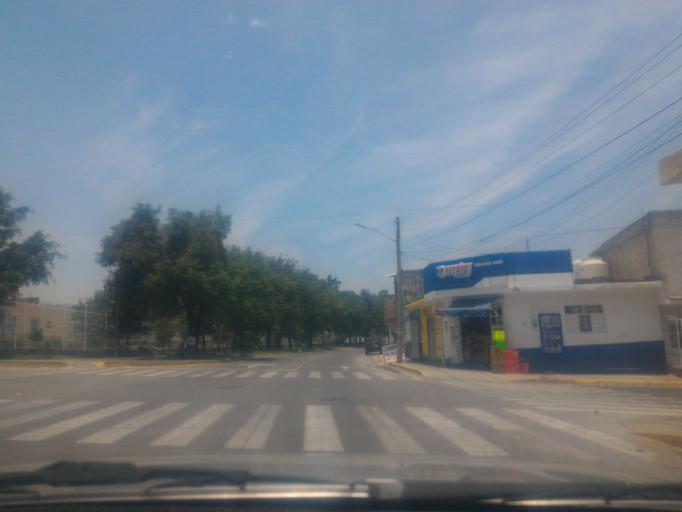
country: MX
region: Jalisco
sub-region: Tlajomulco de Zuniga
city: Altus Bosques
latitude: 20.6202
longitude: -103.3677
